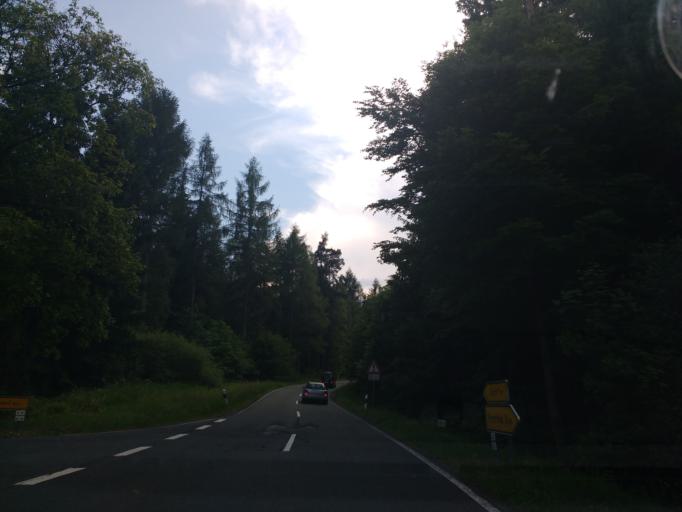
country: DE
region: Hesse
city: Rosenthal
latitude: 50.9561
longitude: 8.8618
